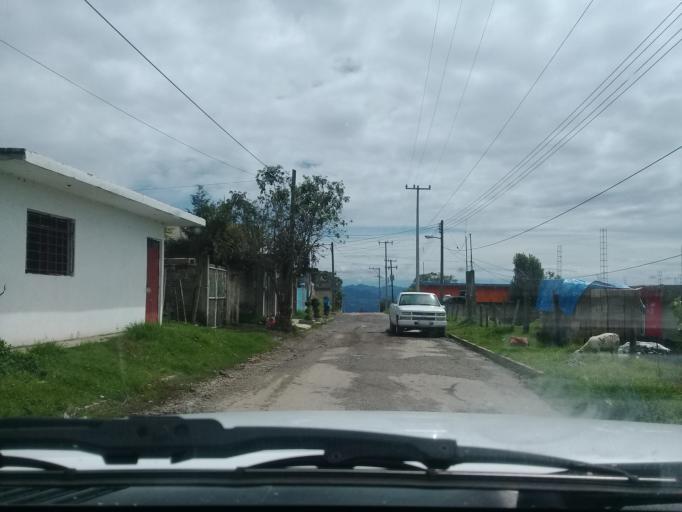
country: MX
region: Veracruz
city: Rafael Lucio
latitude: 19.5935
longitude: -96.9850
